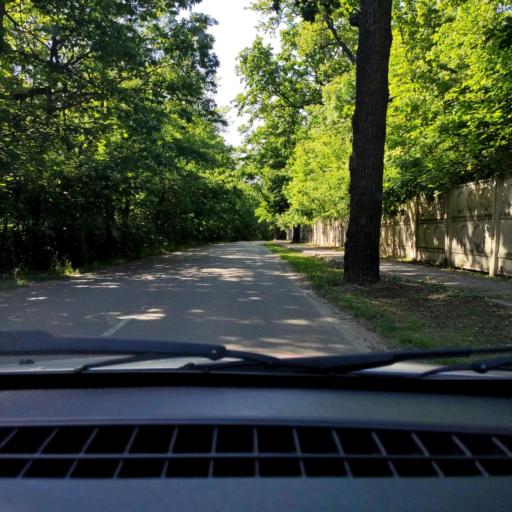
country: RU
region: Voronezj
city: Ramon'
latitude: 51.8227
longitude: 39.2635
